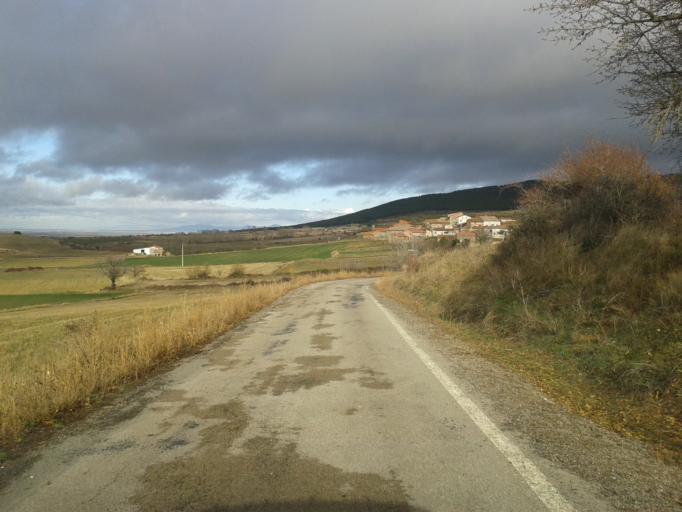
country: ES
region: Aragon
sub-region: Provincia de Teruel
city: Bea
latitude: 40.9863
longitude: -1.1634
